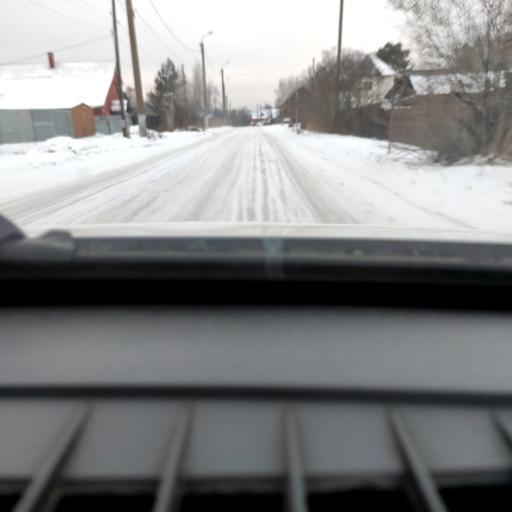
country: RU
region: Perm
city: Perm
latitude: 58.1015
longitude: 56.3693
